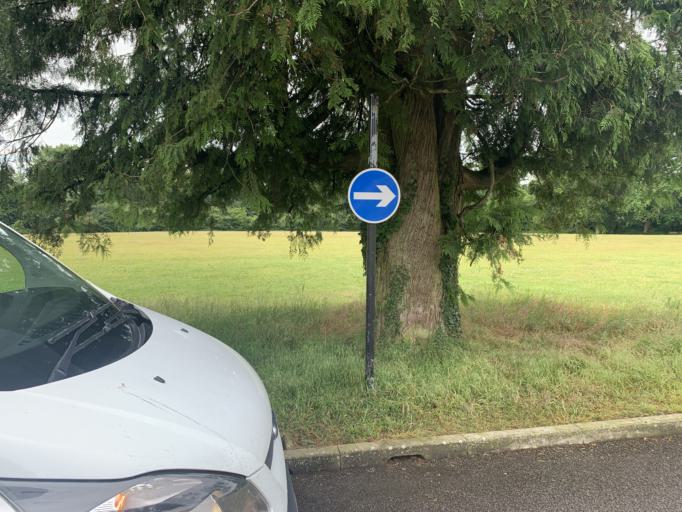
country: GB
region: England
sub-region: Wiltshire
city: Devizes
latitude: 51.3375
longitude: -1.9888
